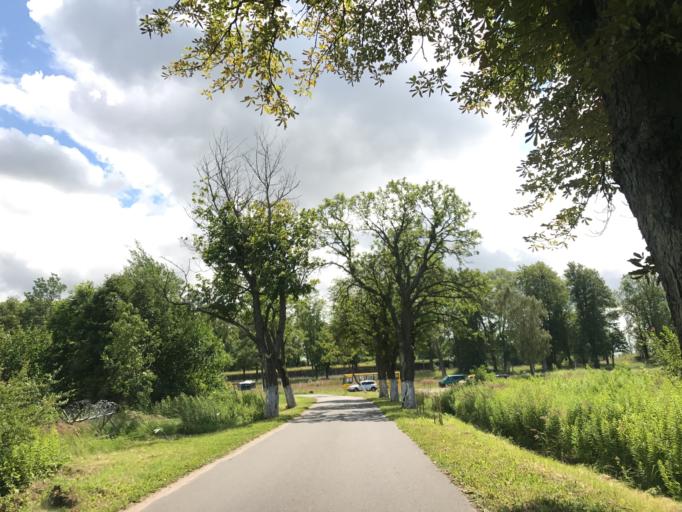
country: RU
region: Kaliningrad
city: Bol'shoe Isakovo
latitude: 54.6587
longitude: 20.5646
